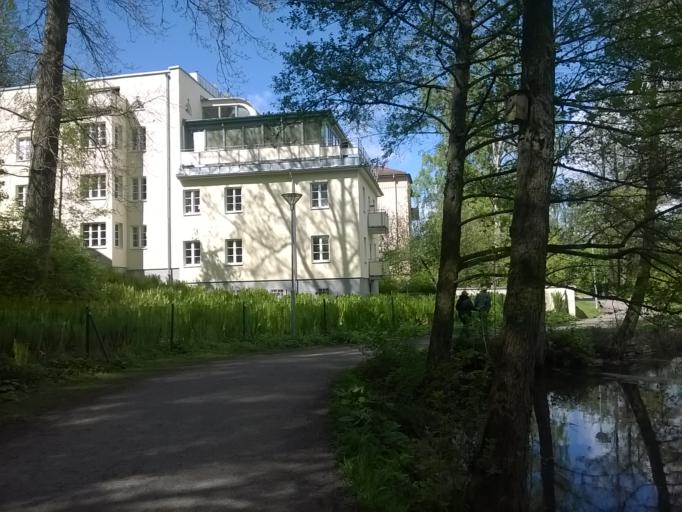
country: SE
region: OEstergoetland
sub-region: Norrkopings Kommun
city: Norrkoping
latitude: 58.5864
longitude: 16.1626
